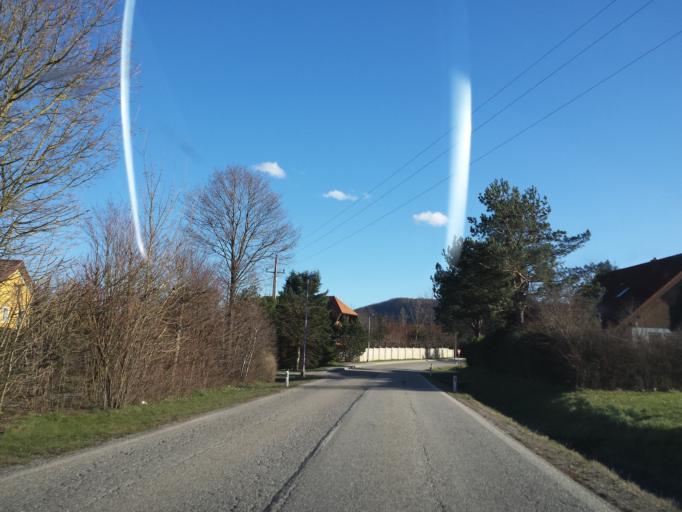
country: AT
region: Styria
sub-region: Politischer Bezirk Graz-Umgebung
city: Sankt Radegund bei Graz
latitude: 47.1449
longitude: 15.4787
